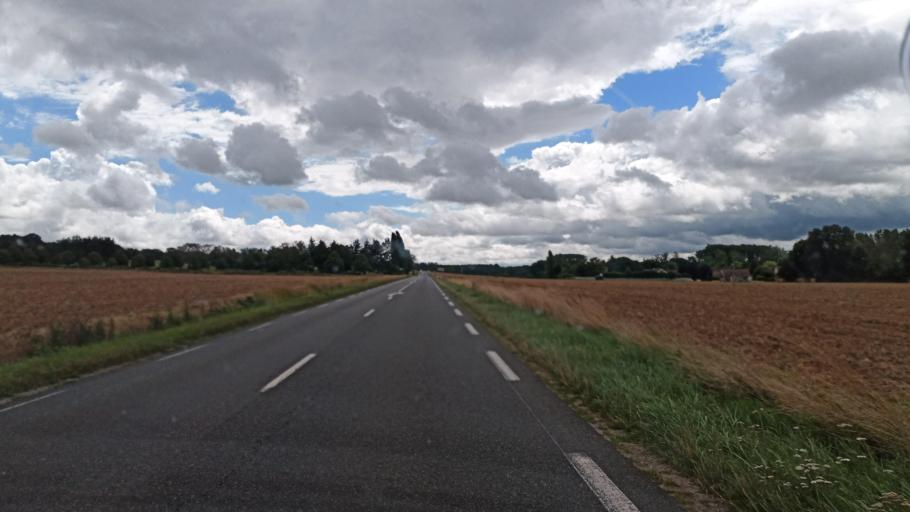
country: FR
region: Ile-de-France
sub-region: Departement de Seine-et-Marne
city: Voulx
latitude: 48.3024
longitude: 2.9477
